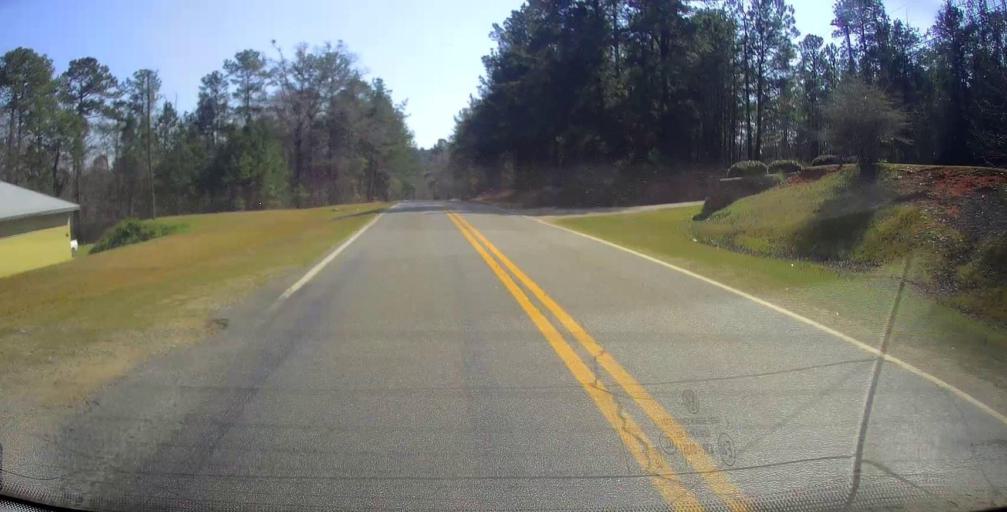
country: US
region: Georgia
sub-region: Jones County
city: Gray
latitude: 32.9303
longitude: -83.5348
